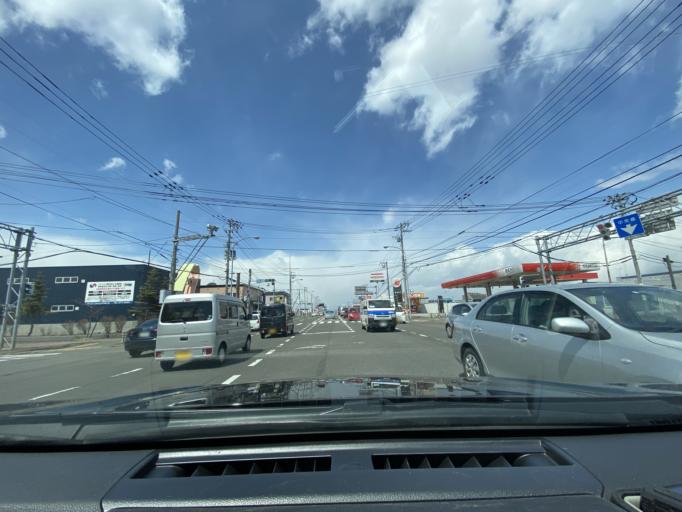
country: JP
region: Hokkaido
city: Kitahiroshima
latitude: 42.9717
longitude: 141.4772
